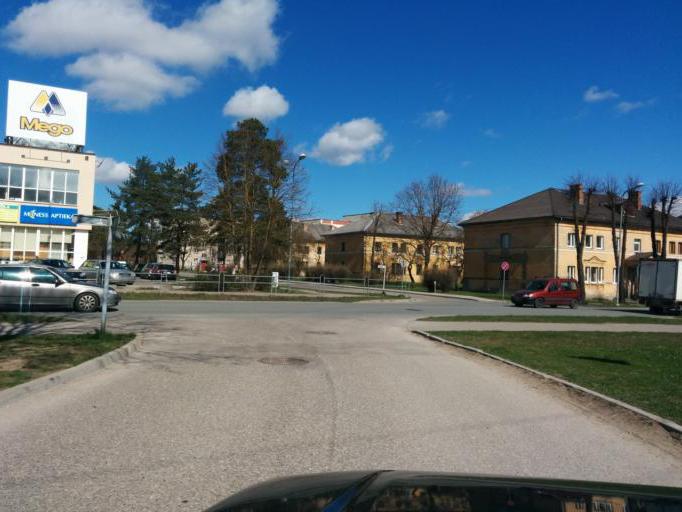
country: LV
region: Kekava
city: Balozi
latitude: 56.8748
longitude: 24.1193
